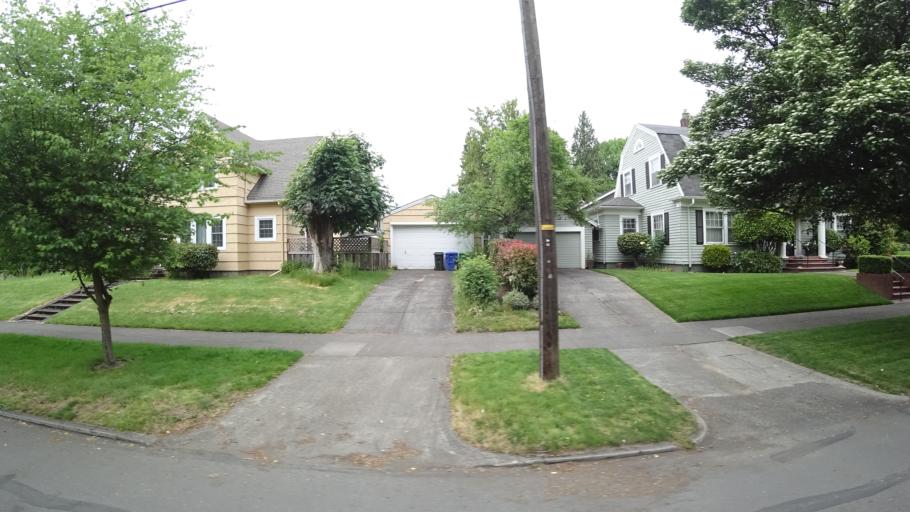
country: US
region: Oregon
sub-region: Multnomah County
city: Portland
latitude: 45.5422
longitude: -122.6529
